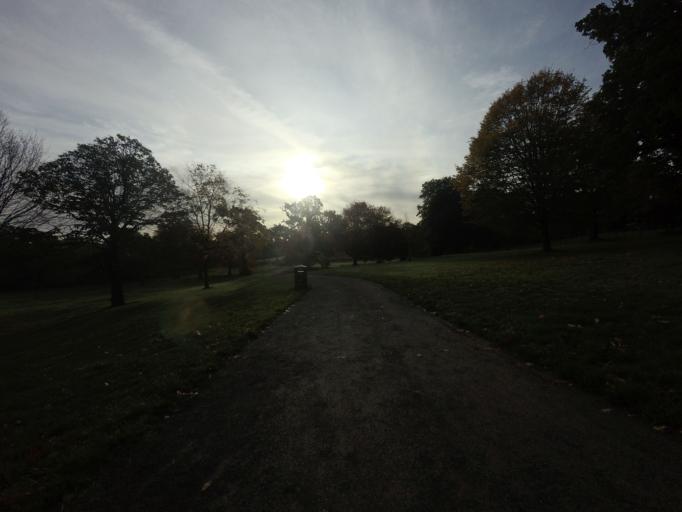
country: GB
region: England
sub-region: Greater London
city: Beckenham
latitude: 51.4214
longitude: -0.0161
